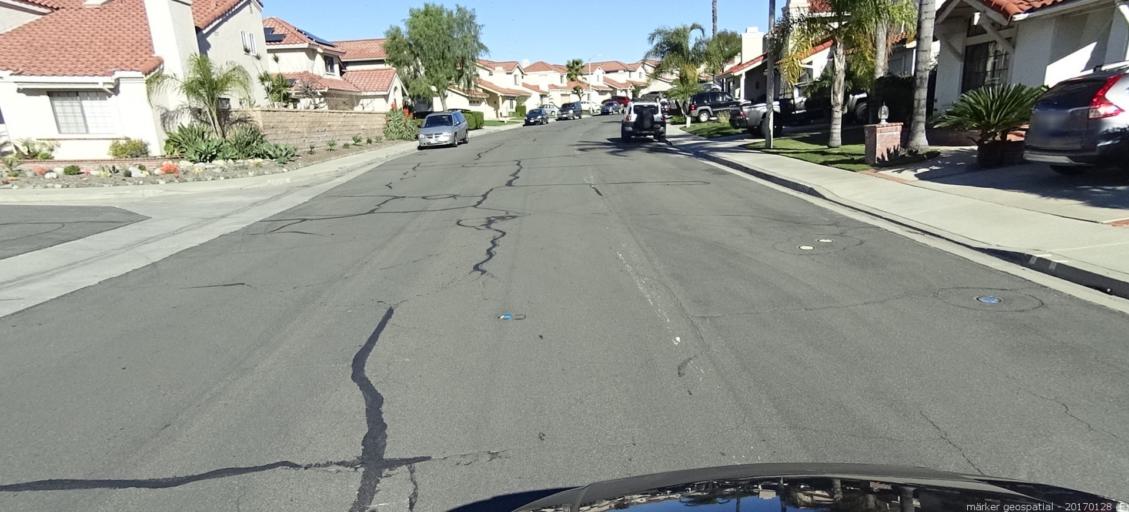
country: US
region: California
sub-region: Orange County
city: Lake Forest
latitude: 33.6495
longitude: -117.6787
